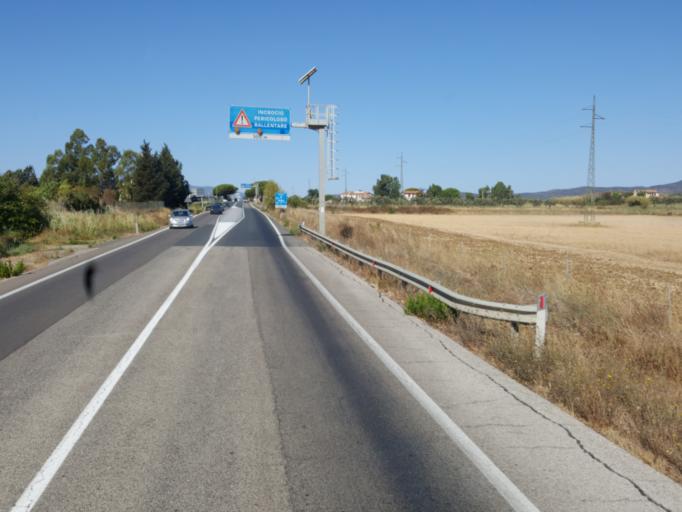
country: IT
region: Tuscany
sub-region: Provincia di Grosseto
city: Capalbio
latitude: 42.4150
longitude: 11.3780
